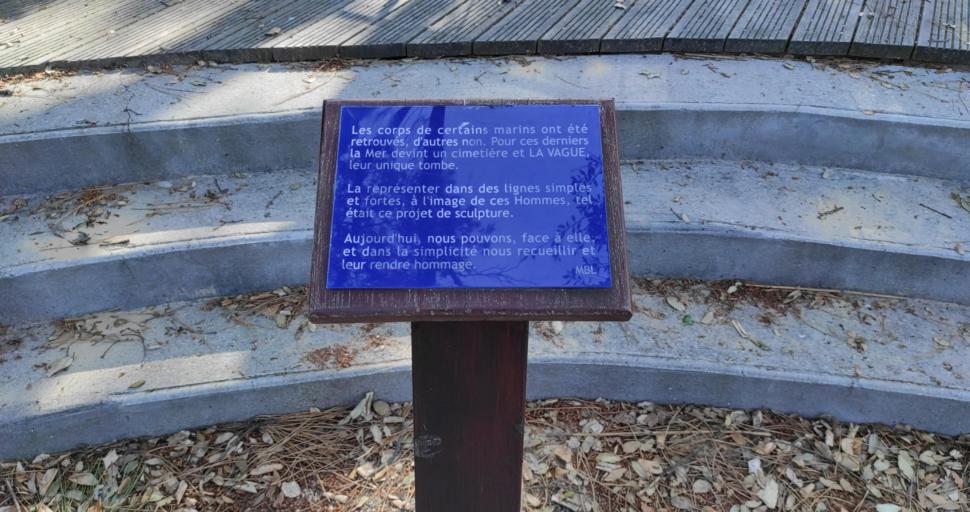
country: FR
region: Aquitaine
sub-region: Departement de la Gironde
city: Arcachon
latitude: 44.6020
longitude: -1.2104
